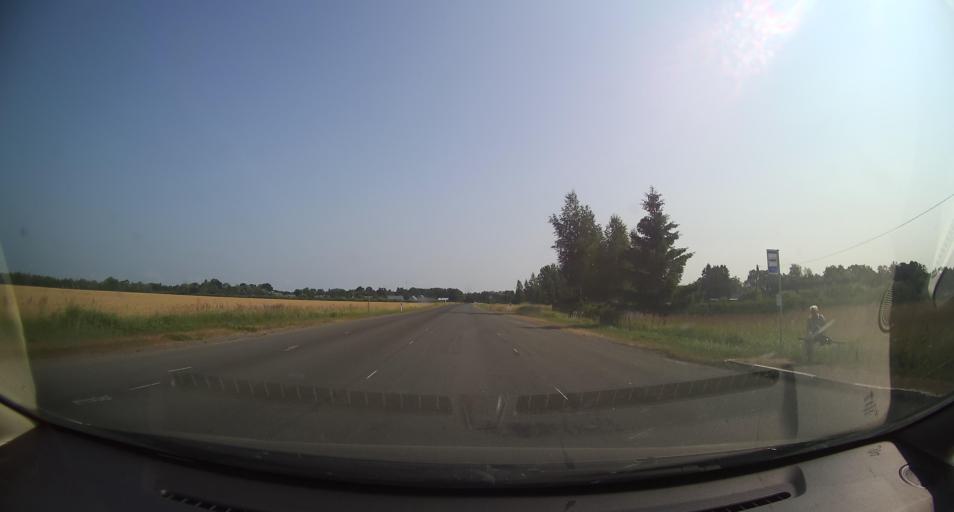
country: EE
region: Paernumaa
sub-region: Audru vald
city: Audru
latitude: 58.4665
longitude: 24.3141
